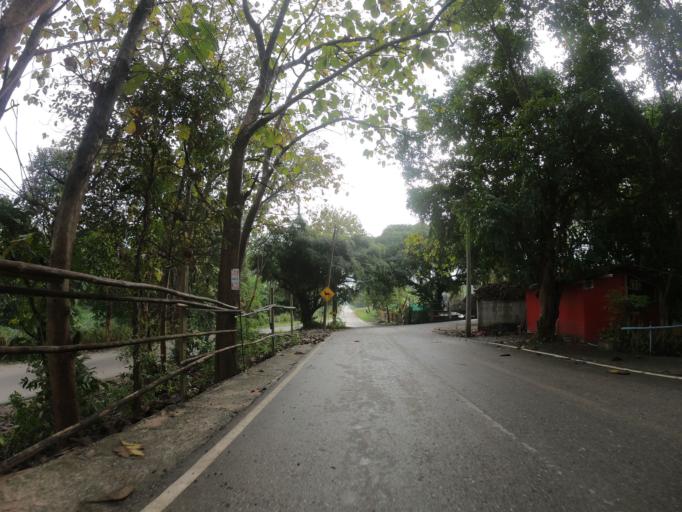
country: TH
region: Chiang Mai
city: Chiang Mai
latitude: 18.8228
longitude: 98.9767
